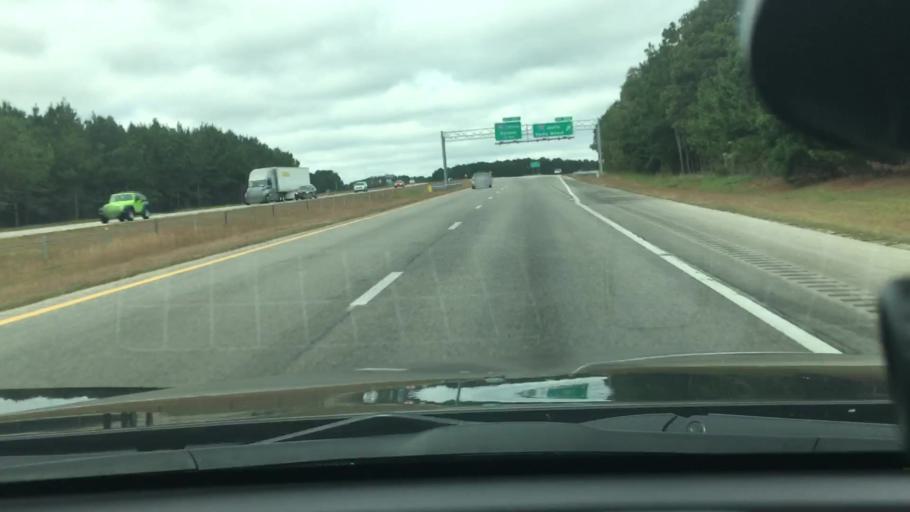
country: US
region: North Carolina
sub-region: Wilson County
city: Lucama
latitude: 35.7284
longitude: -78.0084
